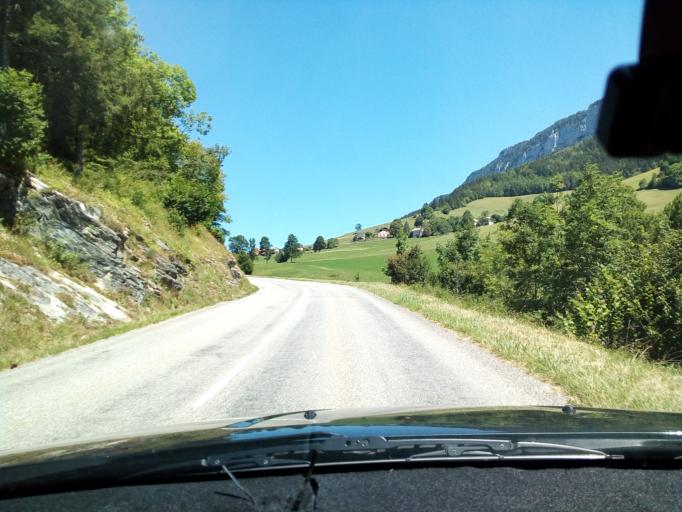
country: FR
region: Rhone-Alpes
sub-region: Departement de l'Isere
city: Pont-en-Royans
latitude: 45.0290
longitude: 5.4439
